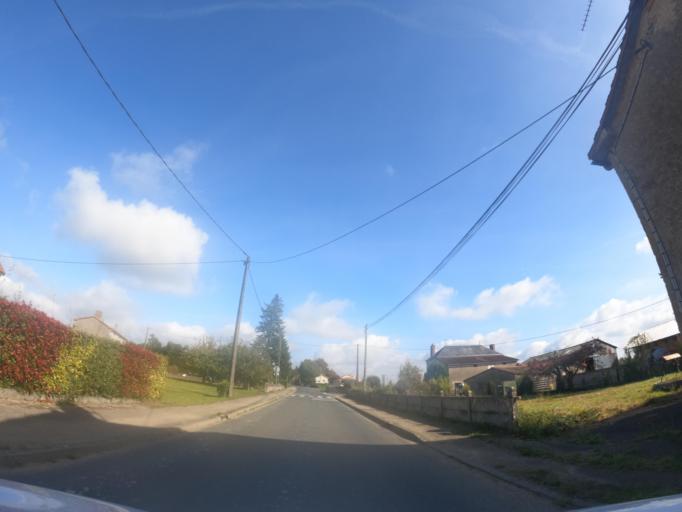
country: FR
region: Poitou-Charentes
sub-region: Departement des Deux-Sevres
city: Courlay
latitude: 46.7799
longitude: -0.5765
